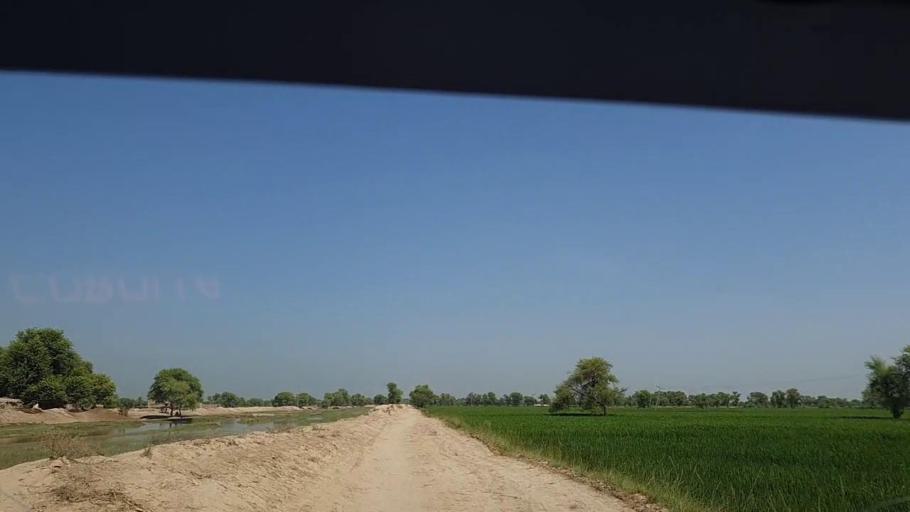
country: PK
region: Sindh
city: Tangwani
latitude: 28.2883
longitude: 69.0436
